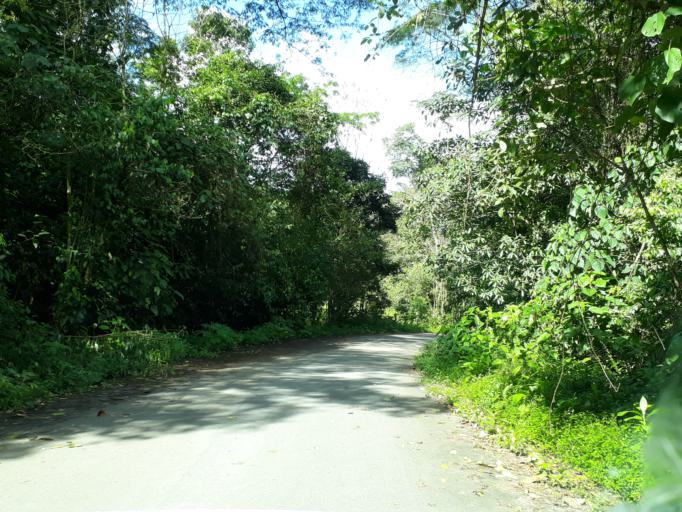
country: CO
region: Boyaca
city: Santa Maria
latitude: 4.7498
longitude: -73.3304
